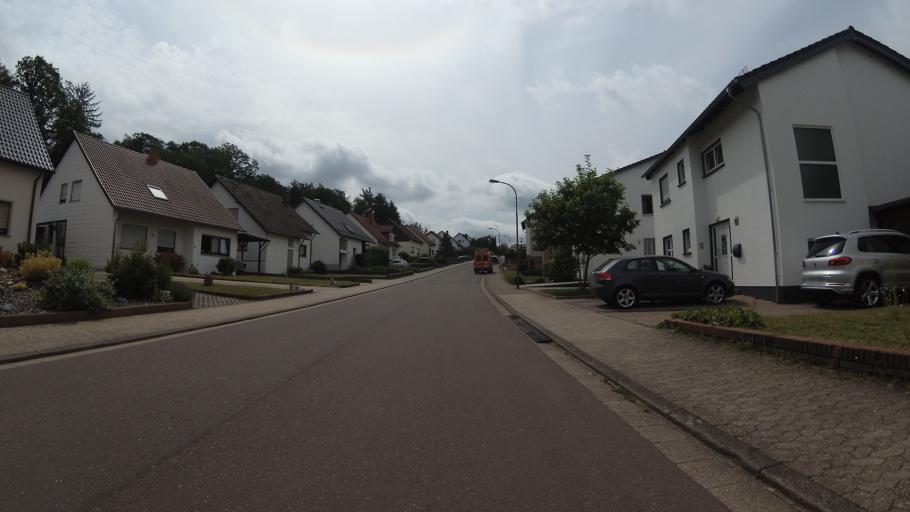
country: DE
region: Saarland
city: Spiesen-Elversberg
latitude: 49.2909
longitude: 7.1659
